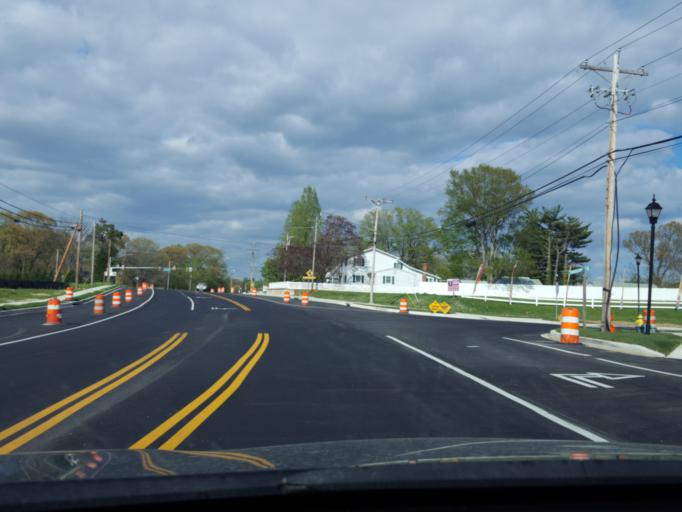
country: US
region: Maryland
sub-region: Calvert County
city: Prince Frederick
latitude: 38.5344
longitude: -76.5930
